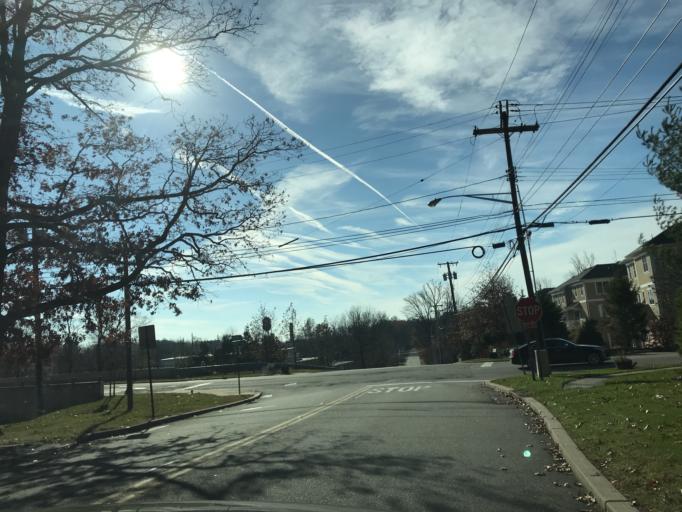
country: US
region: New Jersey
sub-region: Morris County
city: Boonton
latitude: 40.8979
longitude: -74.4180
